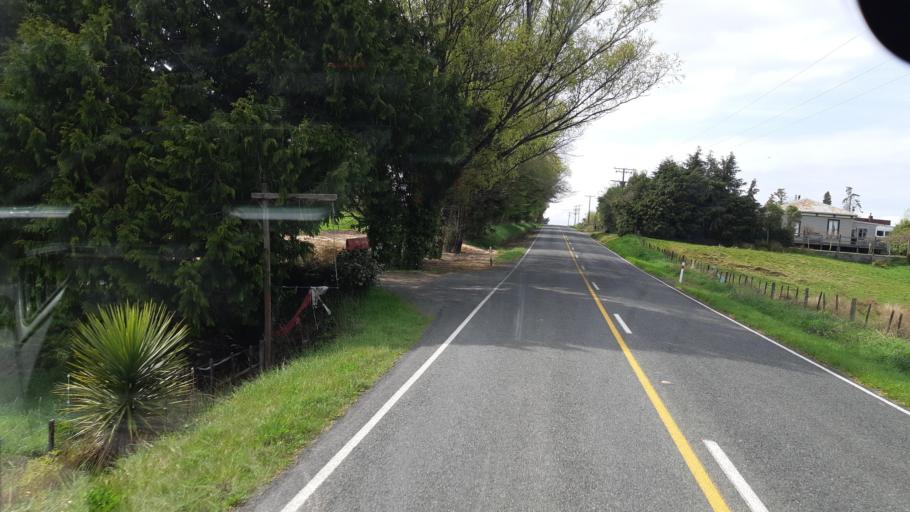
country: NZ
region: Tasman
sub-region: Tasman District
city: Mapua
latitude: -41.2760
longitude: 173.0172
